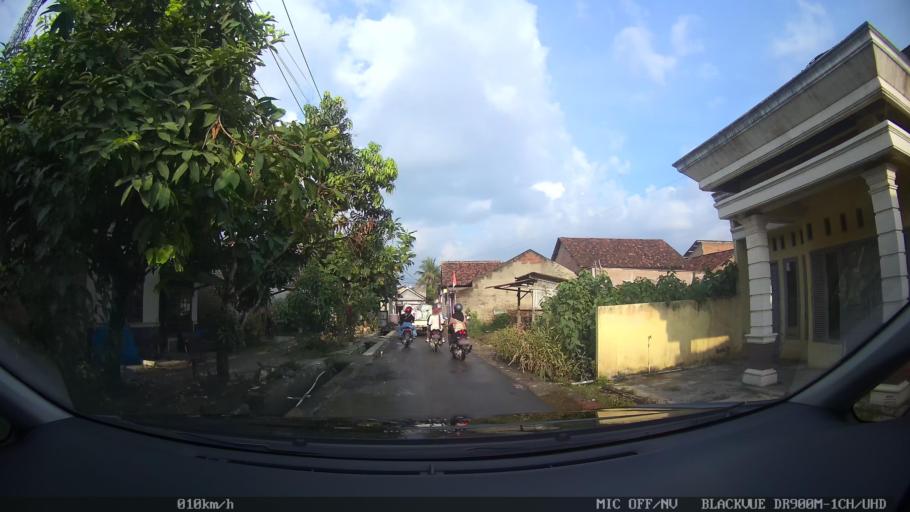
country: ID
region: Lampung
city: Kedaton
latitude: -5.3909
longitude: 105.3148
